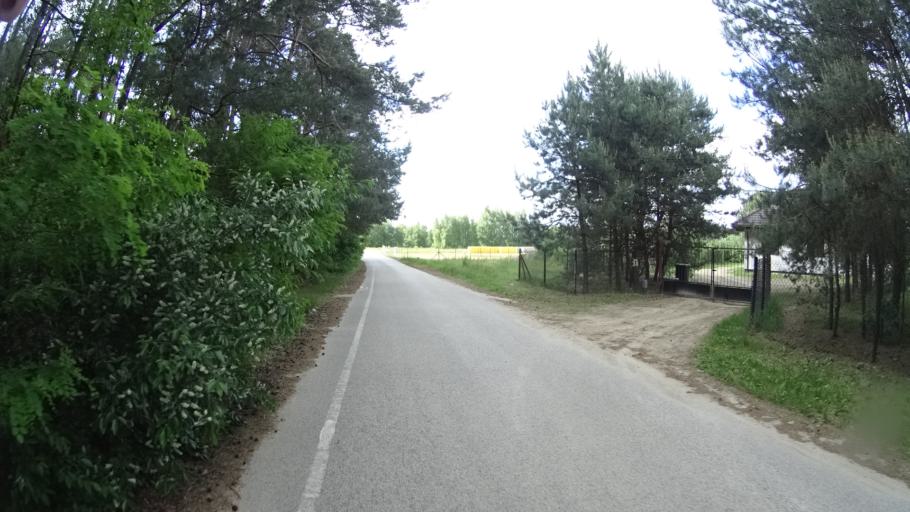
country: PL
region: Masovian Voivodeship
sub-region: Powiat piaseczynski
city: Tarczyn
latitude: 52.0002
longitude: 20.8341
